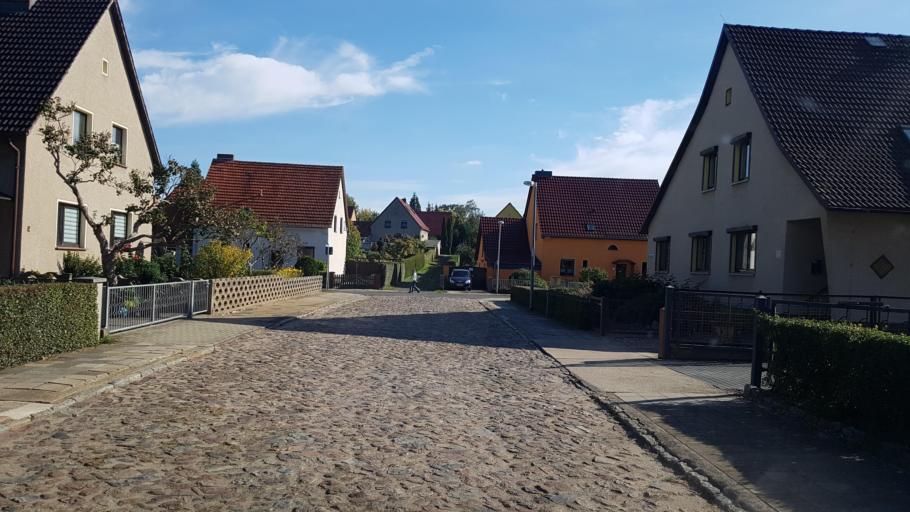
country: DE
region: Brandenburg
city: Belzig
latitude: 52.1453
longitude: 12.6002
